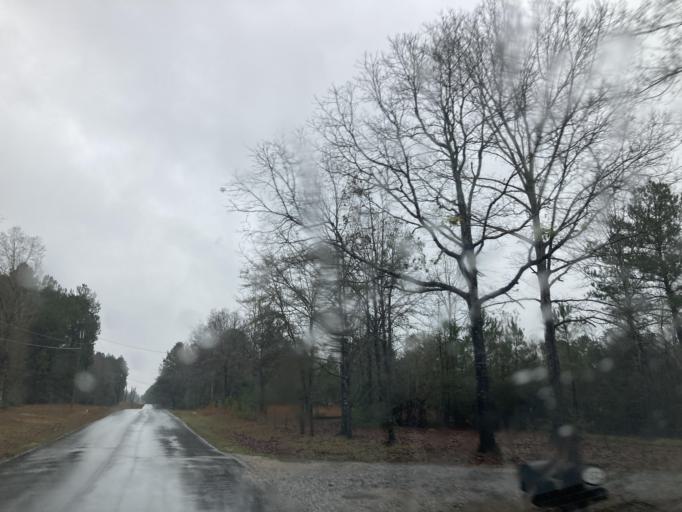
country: US
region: Mississippi
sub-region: Forrest County
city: Rawls Springs
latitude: 31.4731
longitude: -89.3822
